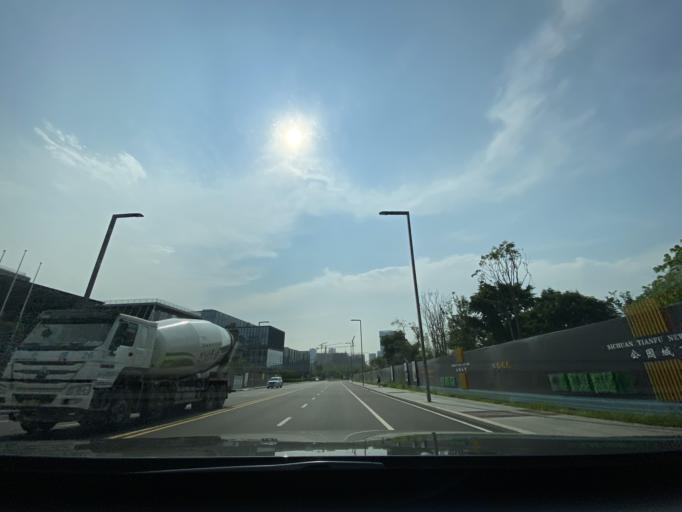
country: CN
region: Sichuan
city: Dongsheng
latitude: 30.3934
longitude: 104.0811
